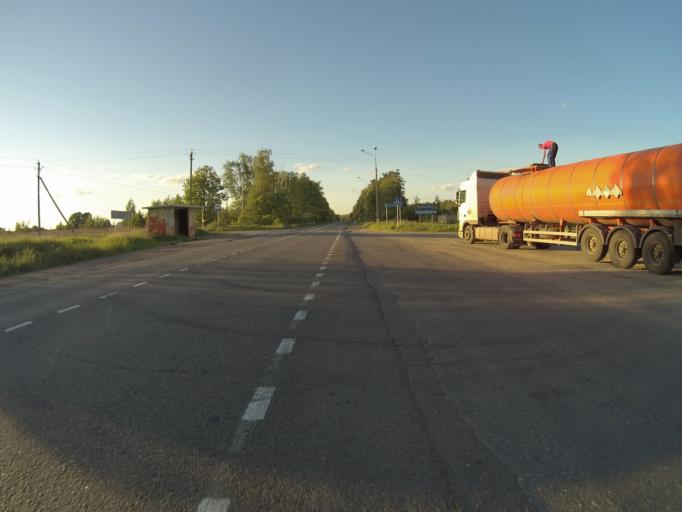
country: RU
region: Vladimir
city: Golovino
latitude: 55.9987
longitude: 40.5639
